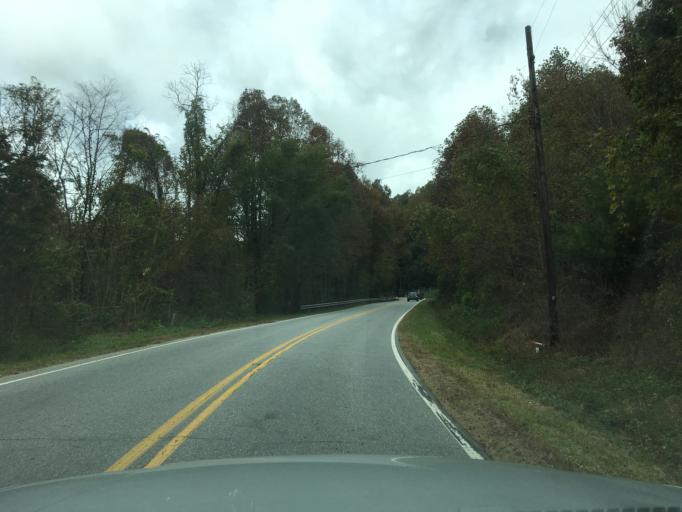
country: US
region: North Carolina
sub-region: Henderson County
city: Flat Rock
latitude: 35.2437
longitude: -82.4189
